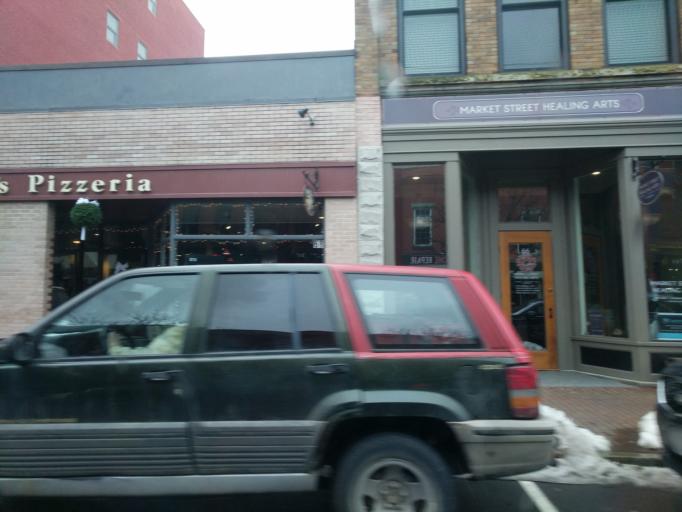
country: US
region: New York
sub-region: Steuben County
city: Corning
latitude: 42.1432
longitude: -77.0521
